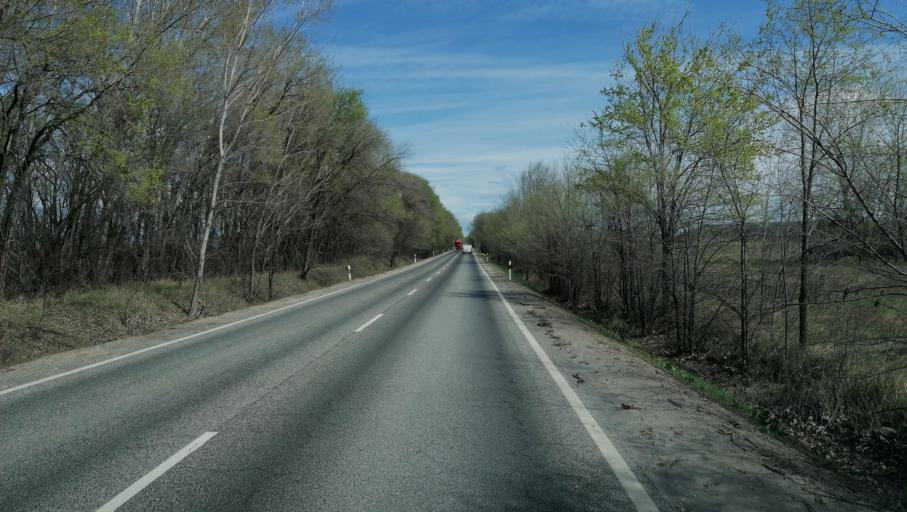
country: HU
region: Pest
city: Alsonemedi
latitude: 47.3064
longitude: 19.1927
